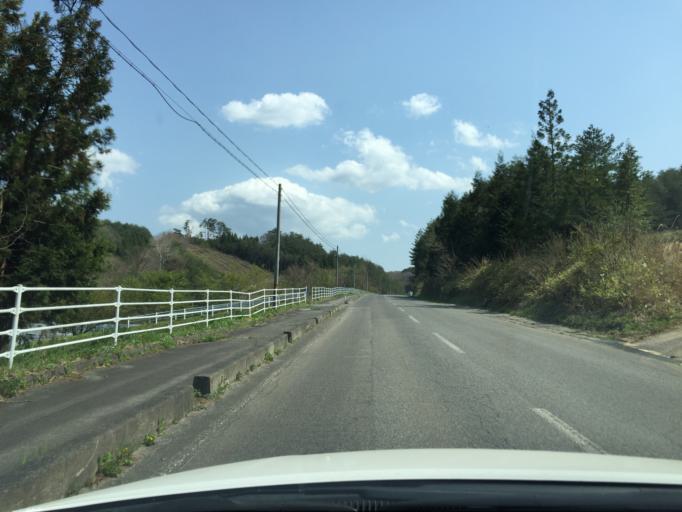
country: JP
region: Fukushima
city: Namie
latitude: 37.4053
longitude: 140.7980
